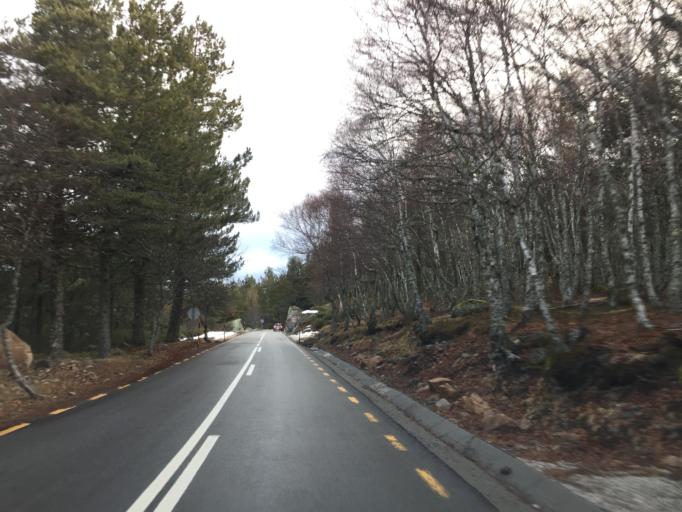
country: PT
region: Castelo Branco
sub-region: Covilha
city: Covilha
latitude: 40.3234
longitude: -7.5727
